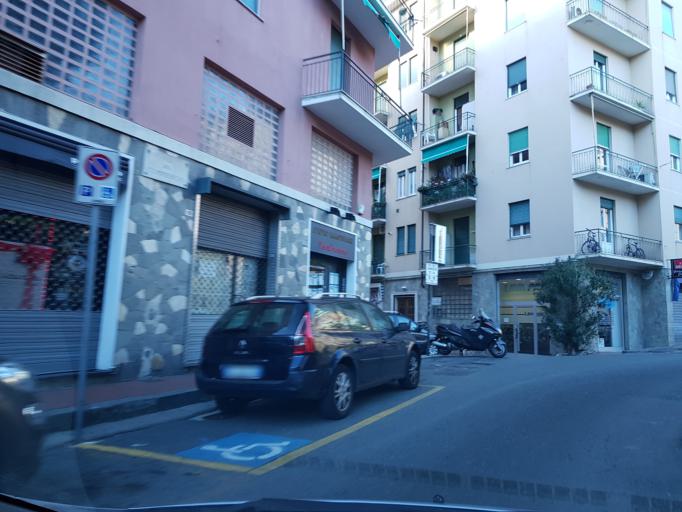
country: IT
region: Liguria
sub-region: Provincia di Genova
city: Bogliasco
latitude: 44.3858
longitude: 9.0326
